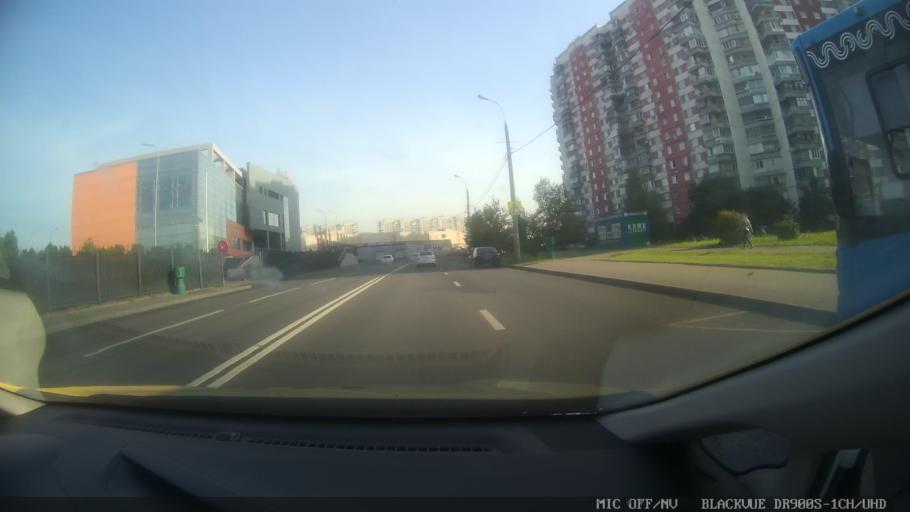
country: RU
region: Moskovskaya
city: Reutov
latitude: 55.7415
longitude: 37.8476
